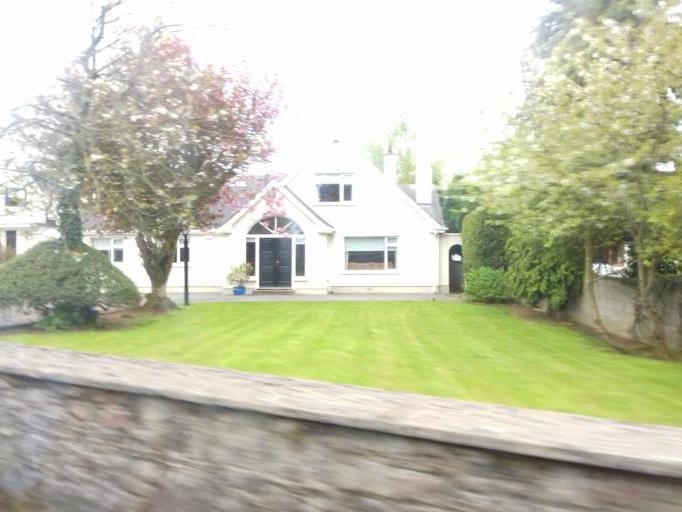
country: IE
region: Leinster
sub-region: Kildare
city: Kildare
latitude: 53.1587
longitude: -6.9155
